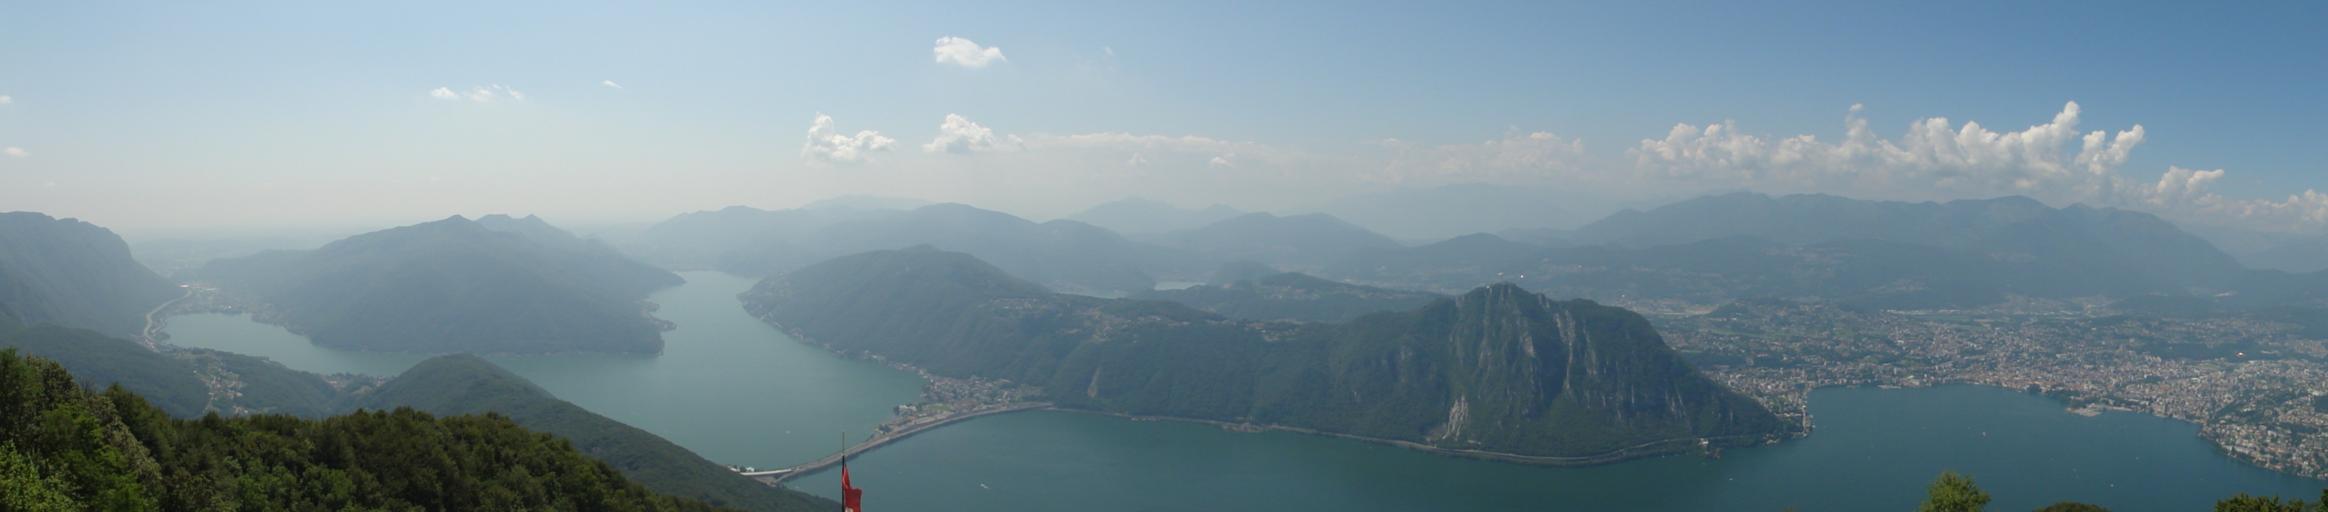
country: IT
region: Lombardy
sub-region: Provincia di Como
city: Campione
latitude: 45.9683
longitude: 8.9918
